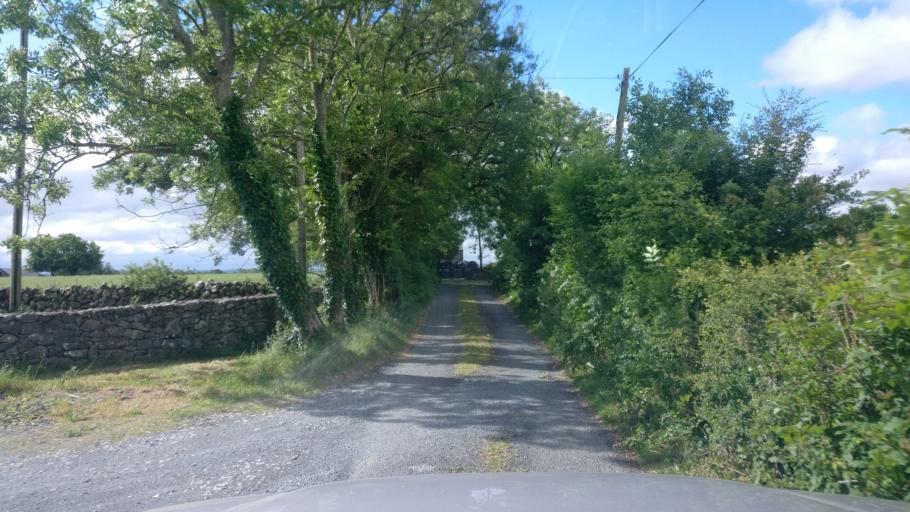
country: IE
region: Connaught
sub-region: County Galway
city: Loughrea
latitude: 53.2335
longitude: -8.6003
